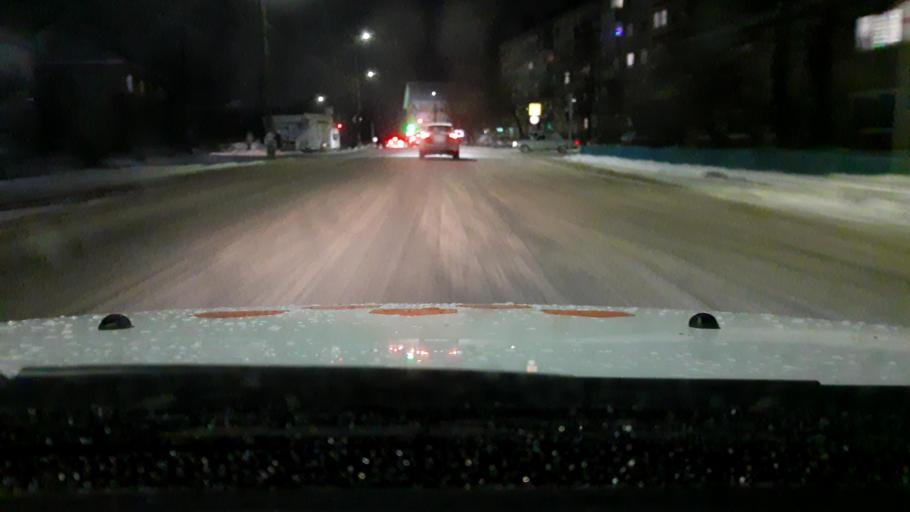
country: RU
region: Nizjnij Novgorod
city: Gorodets
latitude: 56.6657
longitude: 43.4676
